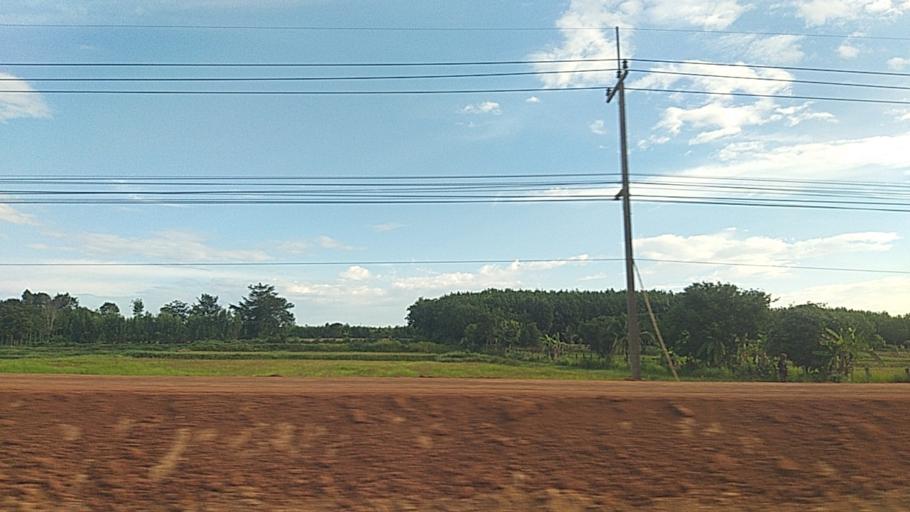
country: TH
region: Surin
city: Kap Choeng
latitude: 14.4642
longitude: 103.6435
